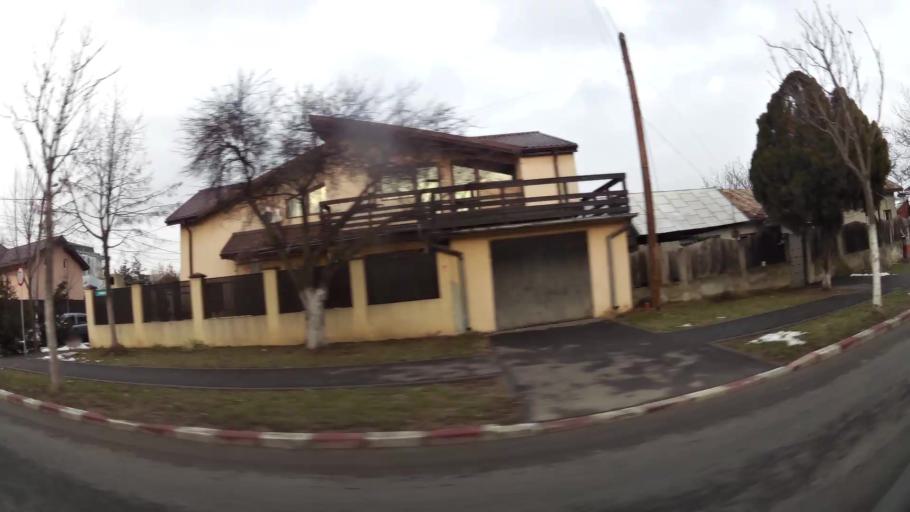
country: RO
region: Ilfov
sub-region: Voluntari City
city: Voluntari
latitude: 44.4877
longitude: 26.1732
